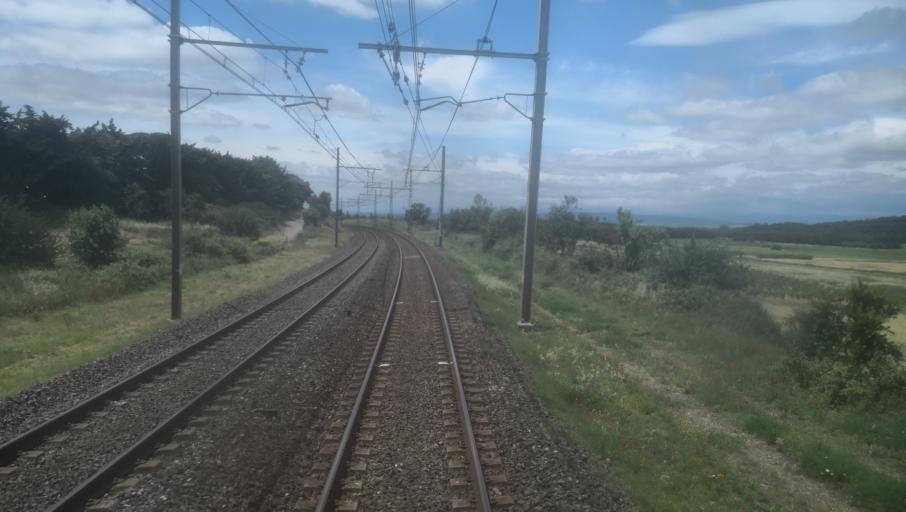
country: FR
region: Languedoc-Roussillon
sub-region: Departement de l'Aude
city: Marcorignan
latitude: 43.2147
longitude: 2.9240
